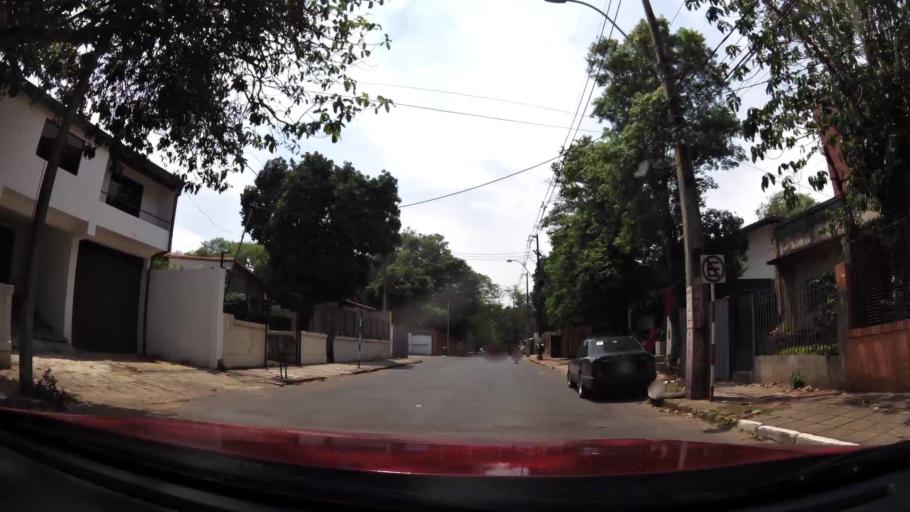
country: PY
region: Asuncion
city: Asuncion
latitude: -25.2840
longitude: -57.5946
